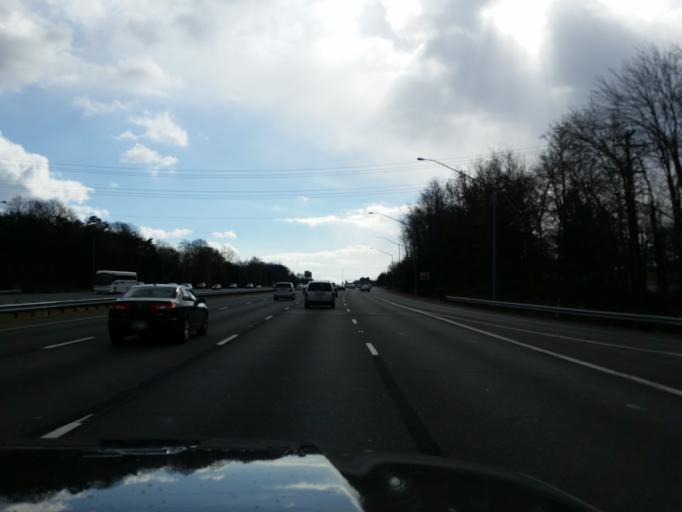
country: US
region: Maryland
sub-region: Prince George's County
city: Berwyn Heights
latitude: 39.0015
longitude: -76.8941
